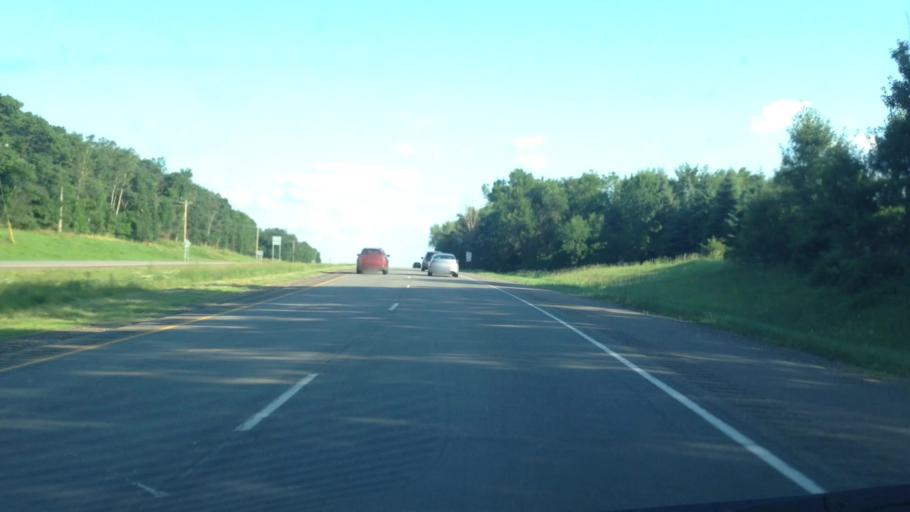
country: US
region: Minnesota
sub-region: Sherburne County
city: Zimmerman
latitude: 45.4031
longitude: -93.5668
